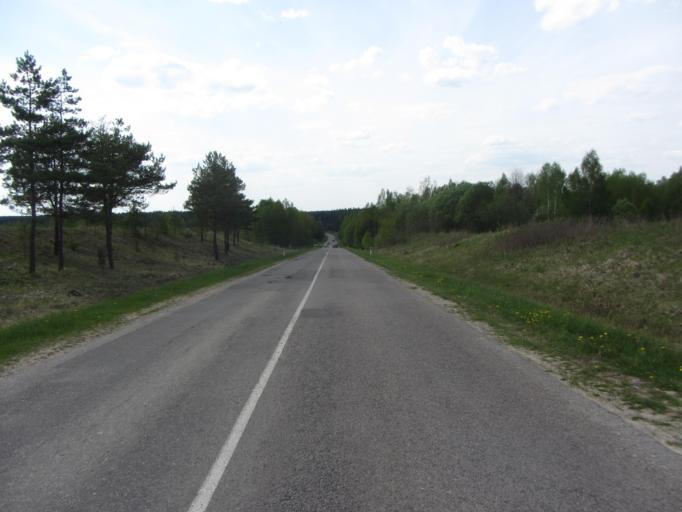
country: LT
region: Utenos apskritis
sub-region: Anyksciai
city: Anyksciai
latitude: 55.4690
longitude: 25.0632
